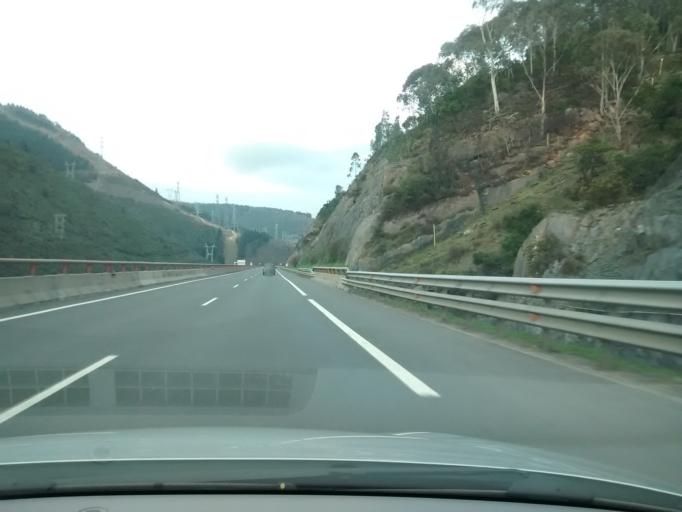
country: ES
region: Basque Country
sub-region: Bizkaia
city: Gordexola
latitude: 43.2097
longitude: -3.0390
